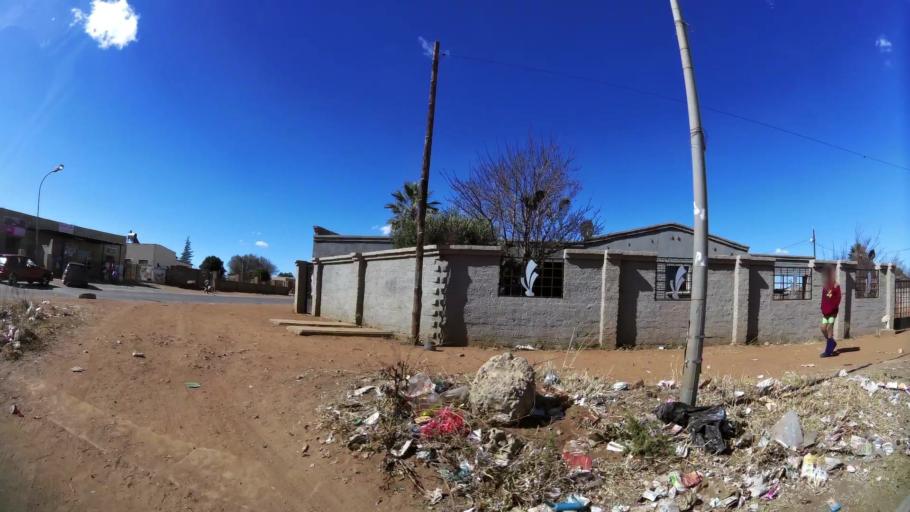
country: ZA
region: North-West
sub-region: Dr Kenneth Kaunda District Municipality
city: Klerksdorp
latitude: -26.8689
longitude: 26.5800
